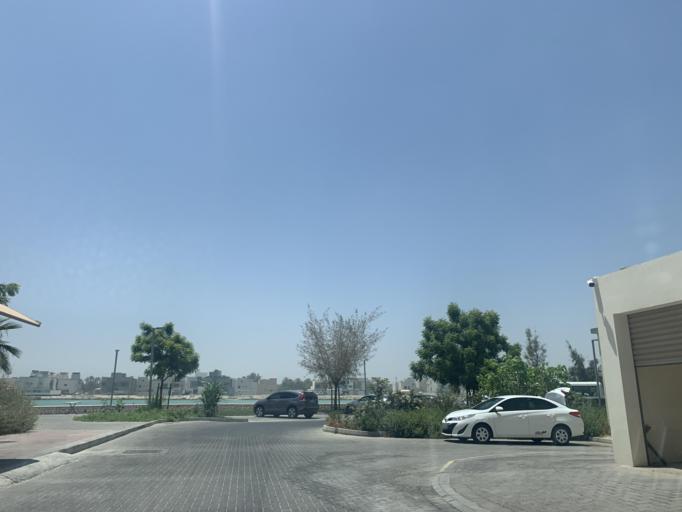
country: BH
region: Manama
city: Jidd Hafs
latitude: 26.2348
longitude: 50.4672
